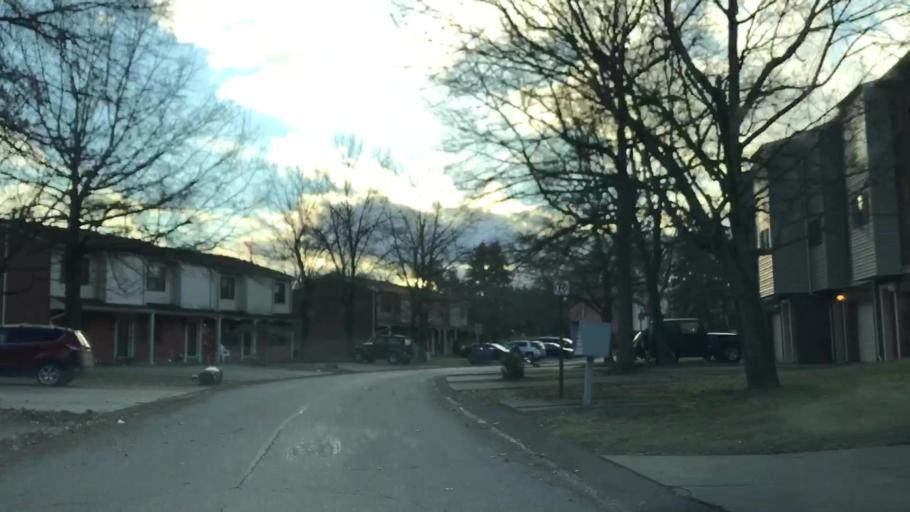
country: US
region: Pennsylvania
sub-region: Butler County
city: Seven Fields
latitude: 40.6858
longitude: -80.0589
